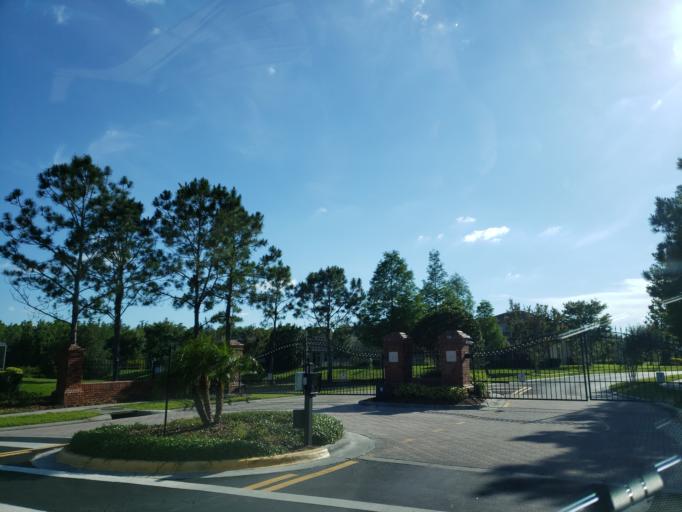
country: US
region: Florida
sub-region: Pasco County
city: Wesley Chapel
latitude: 28.2189
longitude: -82.3570
